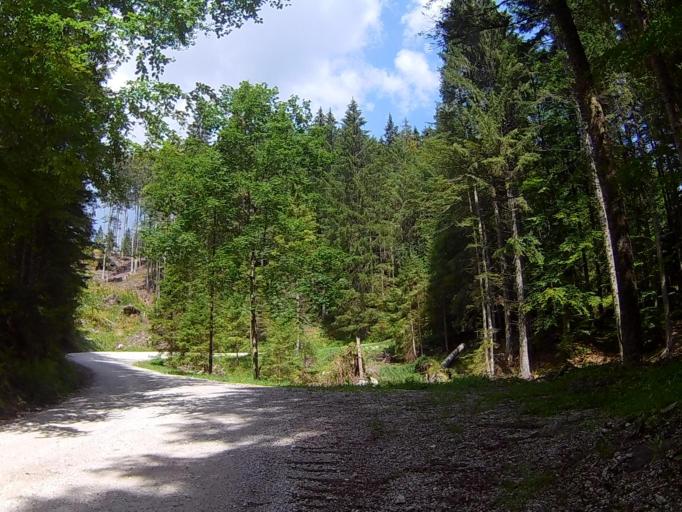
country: SI
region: Lovrenc na Pohorju
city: Lovrenc na Pohorju
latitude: 46.4814
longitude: 15.4445
